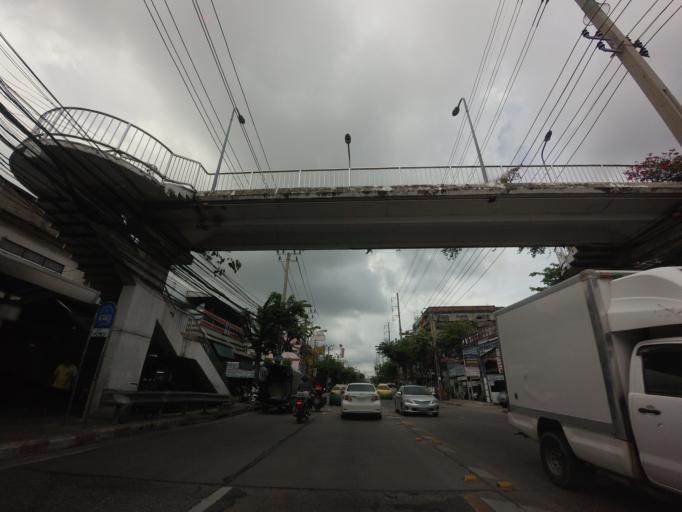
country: TH
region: Bangkok
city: Rat Burana
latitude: 13.6662
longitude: 100.5042
